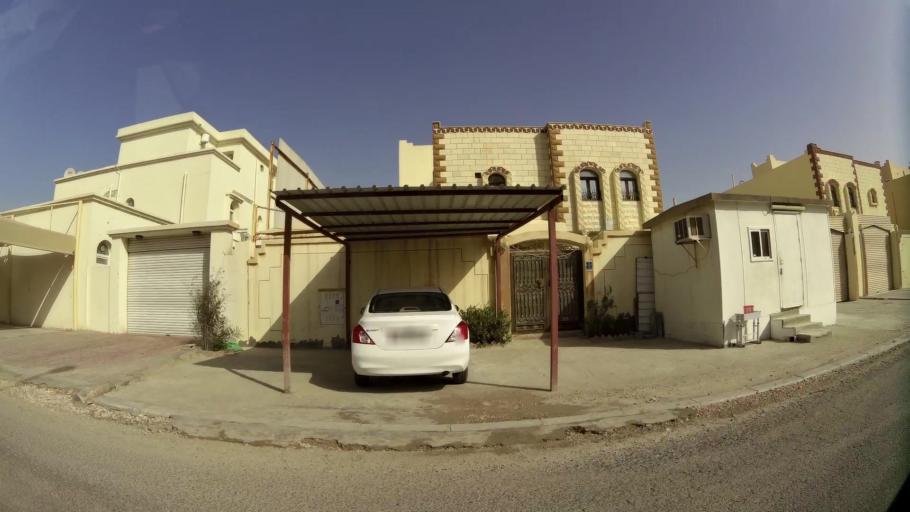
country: QA
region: Baladiyat ar Rayyan
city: Ar Rayyan
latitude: 25.3385
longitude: 51.4268
